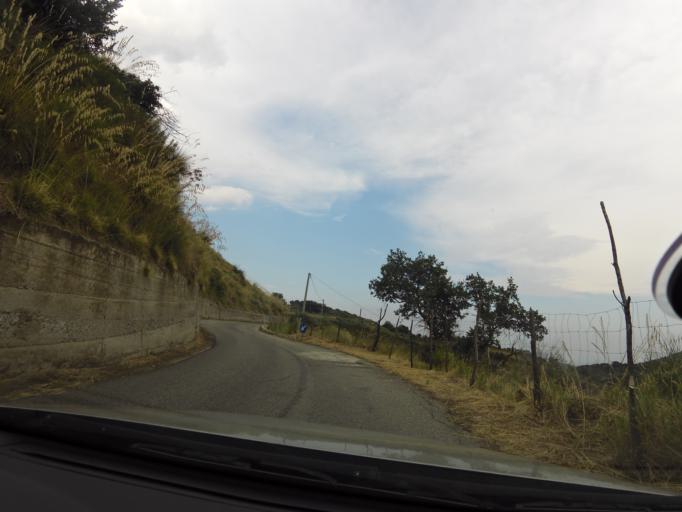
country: IT
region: Calabria
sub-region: Provincia di Reggio Calabria
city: Pazzano
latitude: 38.4614
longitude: 16.4513
